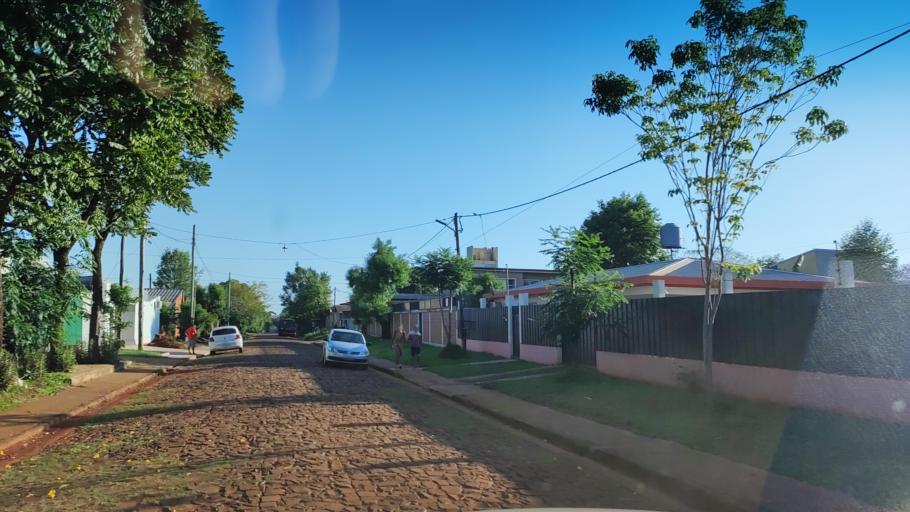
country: AR
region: Misiones
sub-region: Departamento de Capital
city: Posadas
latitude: -27.3747
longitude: -55.9422
